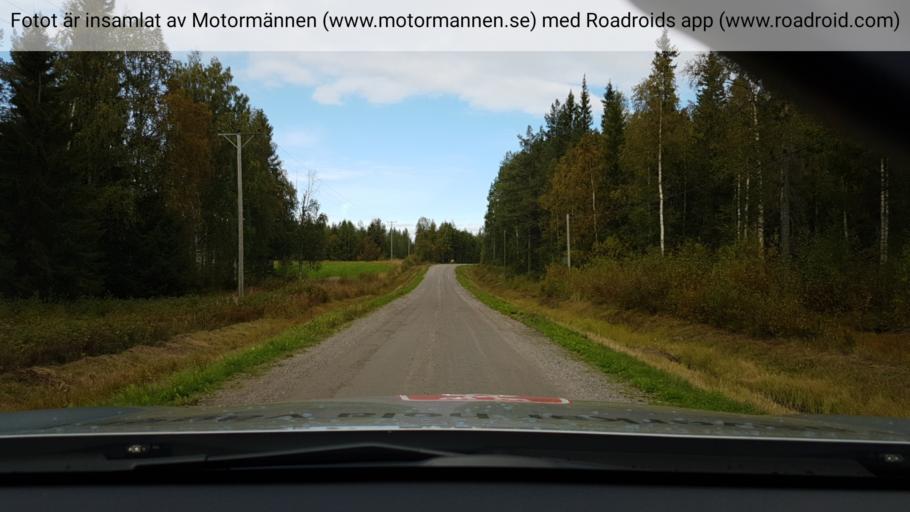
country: SE
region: Vaesterbotten
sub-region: Skelleftea Kommun
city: Backa
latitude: 65.1518
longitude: 21.1624
